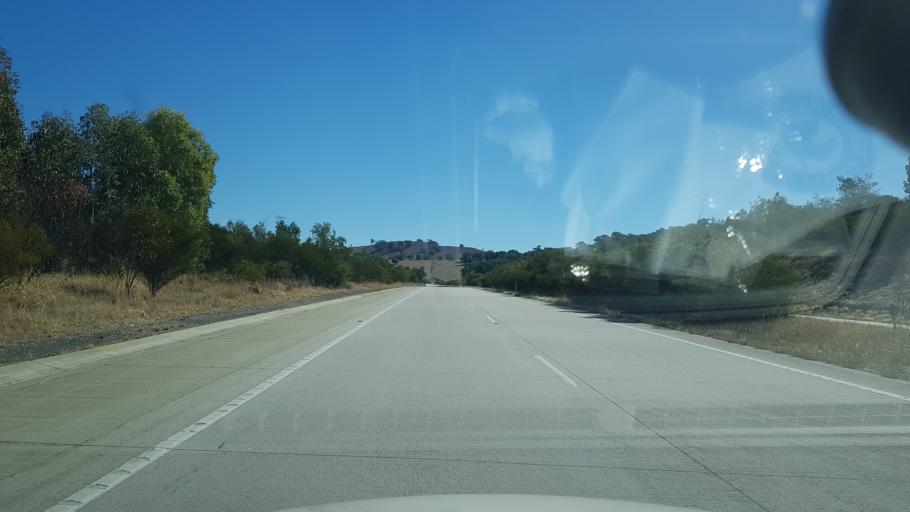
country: AU
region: New South Wales
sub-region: Albury Municipality
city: Lavington
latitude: -35.9155
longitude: 147.1095
